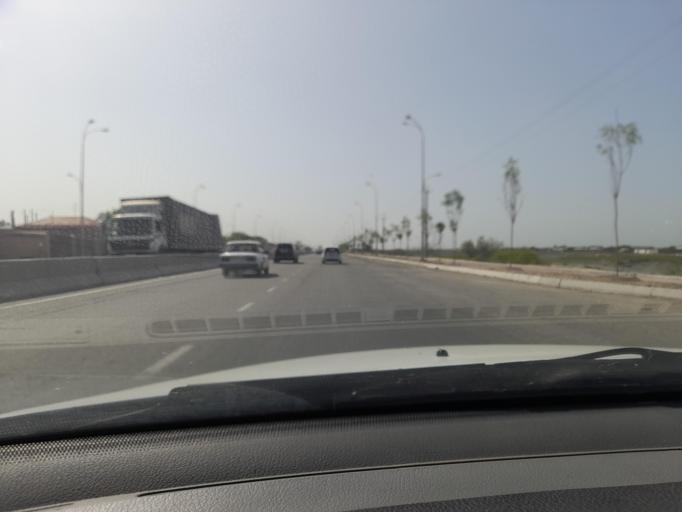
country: UZ
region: Samarqand
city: Samarqand
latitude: 39.7093
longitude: 66.9840
